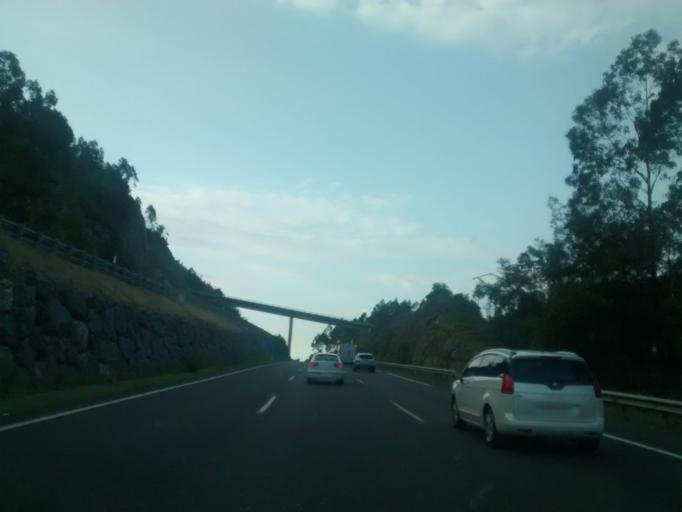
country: ES
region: Cantabria
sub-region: Provincia de Cantabria
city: Los Corrales de Buelna
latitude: 43.2928
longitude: -4.0781
